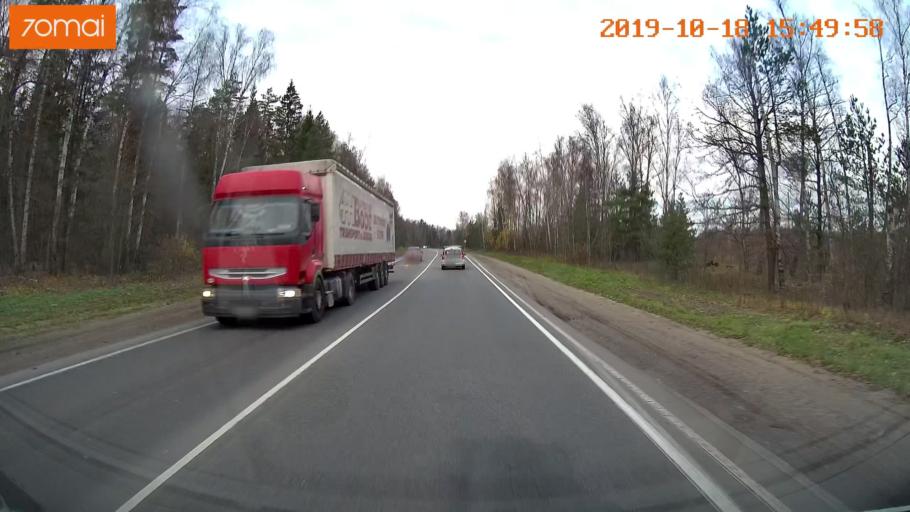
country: RU
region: Vladimir
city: Kommunar
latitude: 56.0283
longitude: 40.5666
